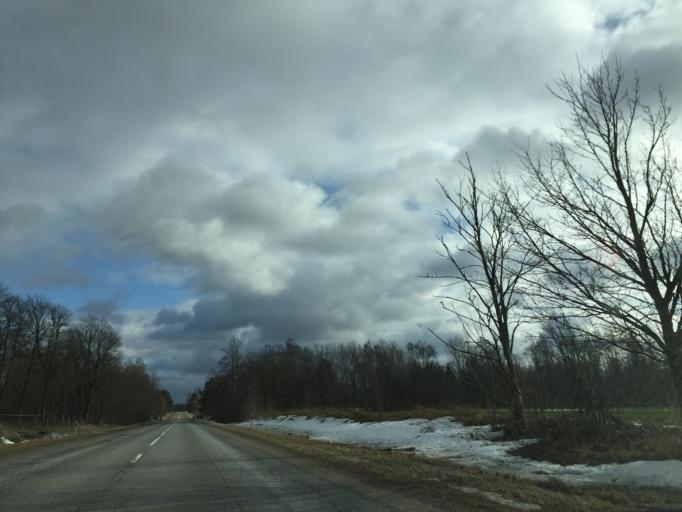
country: LV
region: Aloja
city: Staicele
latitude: 57.8937
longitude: 24.6385
